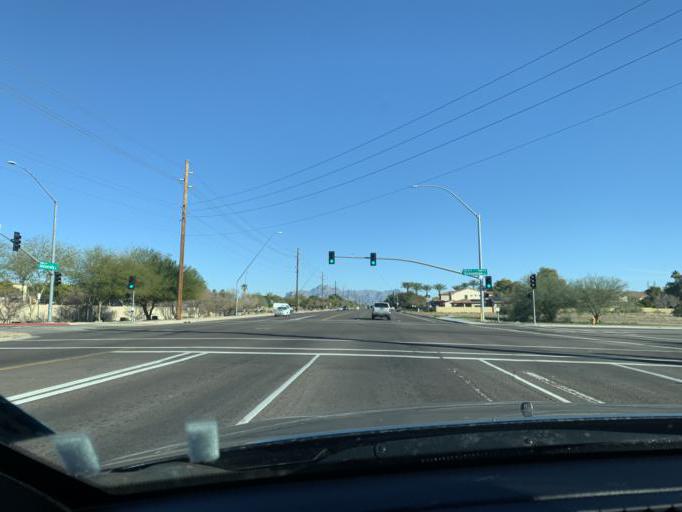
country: US
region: Arizona
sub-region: Pinal County
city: Apache Junction
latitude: 33.4224
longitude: -111.6677
